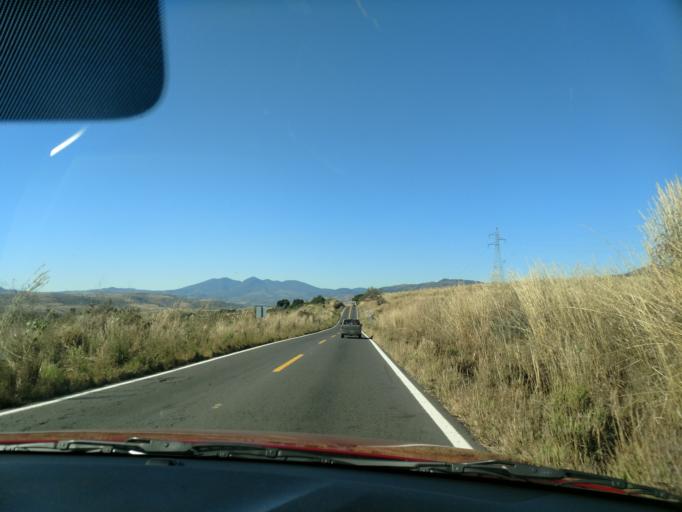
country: MX
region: Nayarit
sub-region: Ahuacatlan
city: Ahuacatlan
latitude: 21.1171
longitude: -104.5915
